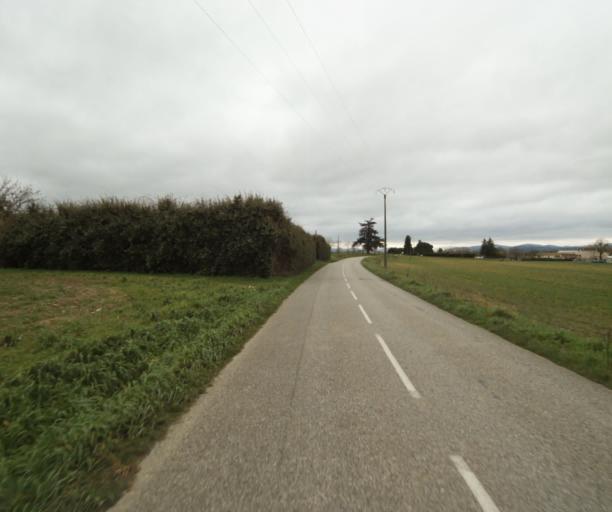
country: FR
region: Midi-Pyrenees
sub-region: Departement de l'Ariege
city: Pamiers
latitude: 43.1678
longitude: 1.6362
